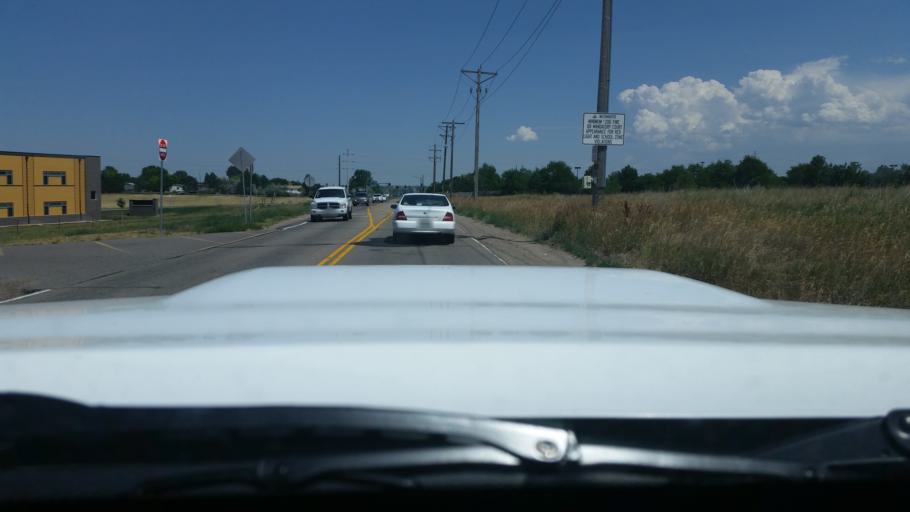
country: US
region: Colorado
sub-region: Broomfield County
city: Broomfield
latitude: 39.8998
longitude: -105.0762
